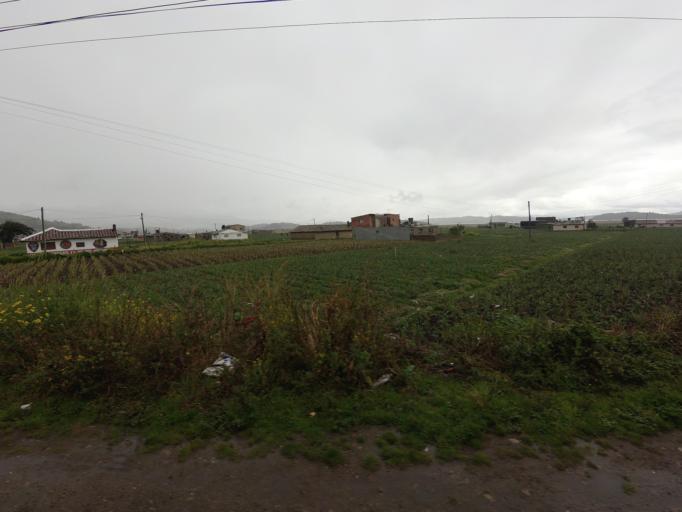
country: CO
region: Boyaca
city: Aquitania
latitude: 5.5268
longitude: -72.8837
